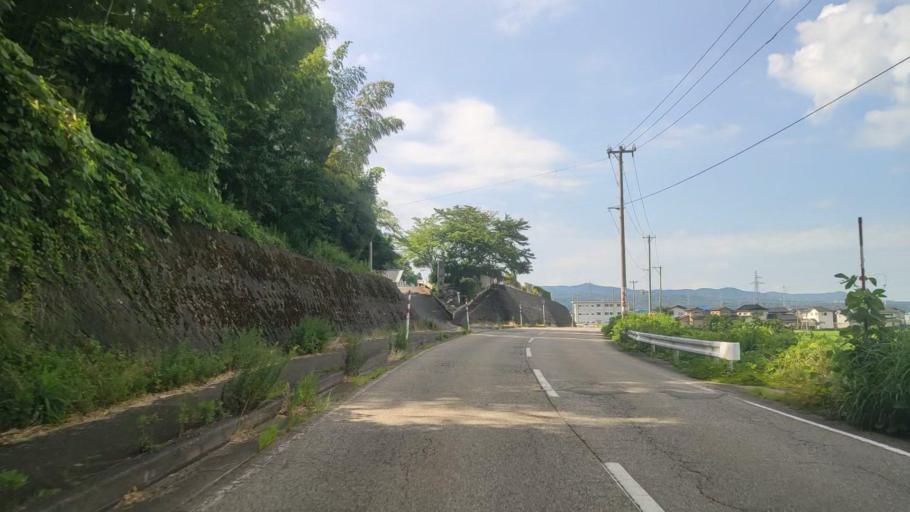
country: JP
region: Ishikawa
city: Tsurugi-asahimachi
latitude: 36.4789
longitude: 136.6162
